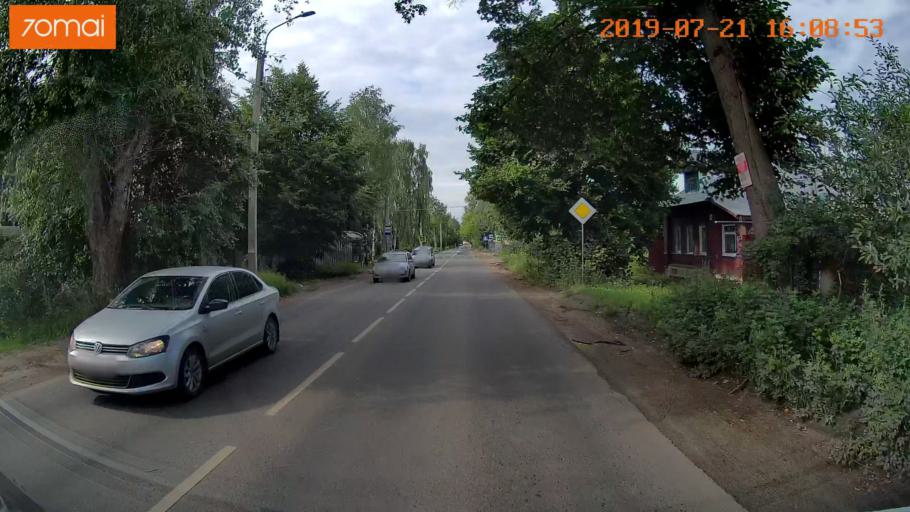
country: RU
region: Ivanovo
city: Bogorodskoye
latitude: 56.9997
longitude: 41.0295
